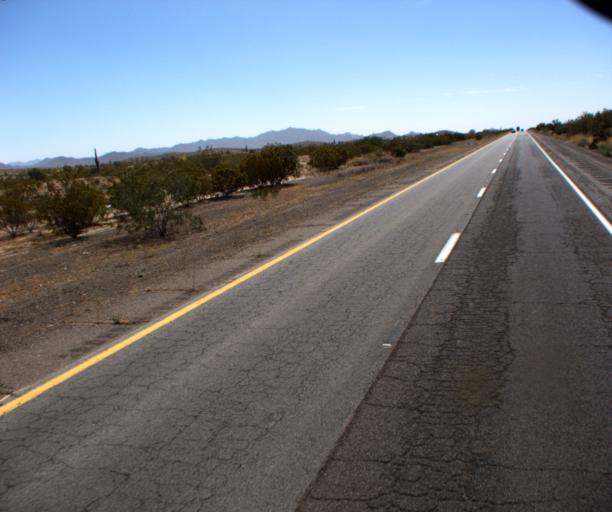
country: US
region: Arizona
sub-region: Maricopa County
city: Buckeye
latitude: 33.2738
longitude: -112.6328
